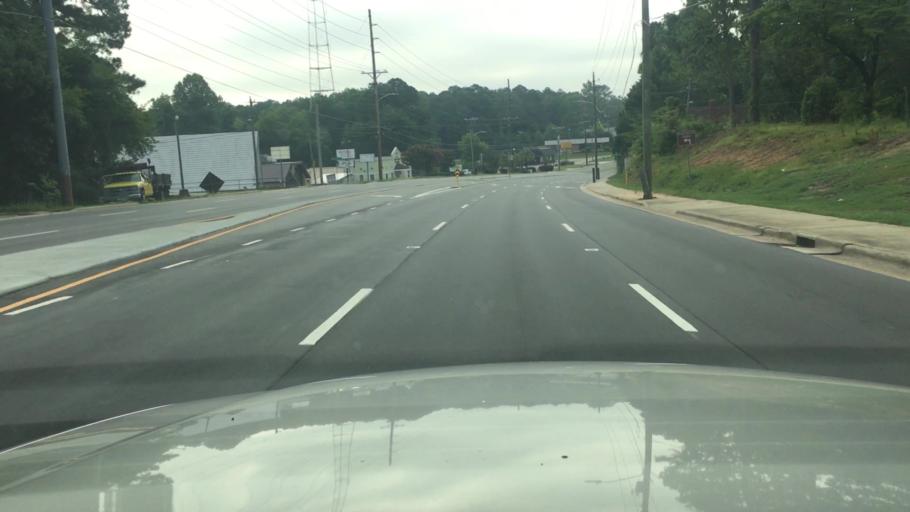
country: US
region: North Carolina
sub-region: Cumberland County
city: Fayetteville
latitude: 35.0685
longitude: -78.9057
